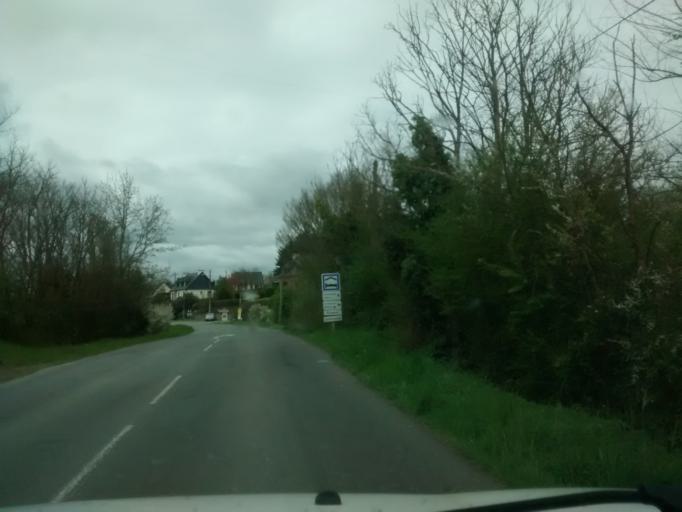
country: FR
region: Brittany
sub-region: Departement d'Ille-et-Vilaine
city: Saint-Jouan-des-Guerets
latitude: 48.5743
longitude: -1.9611
